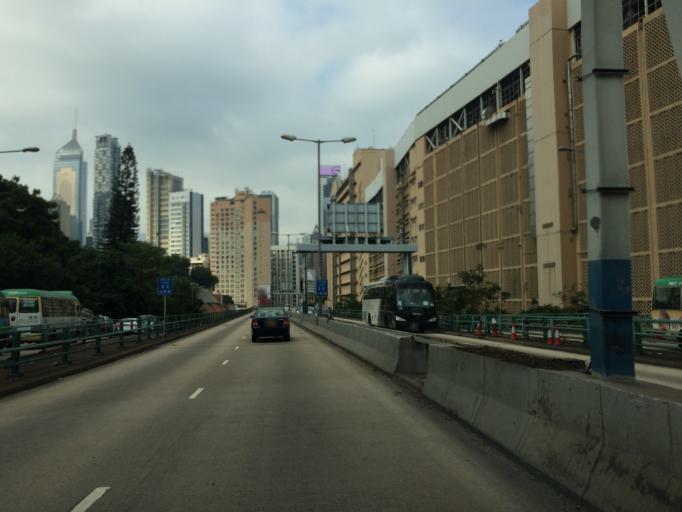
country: HK
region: Wanchai
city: Wan Chai
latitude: 22.2716
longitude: 114.1802
